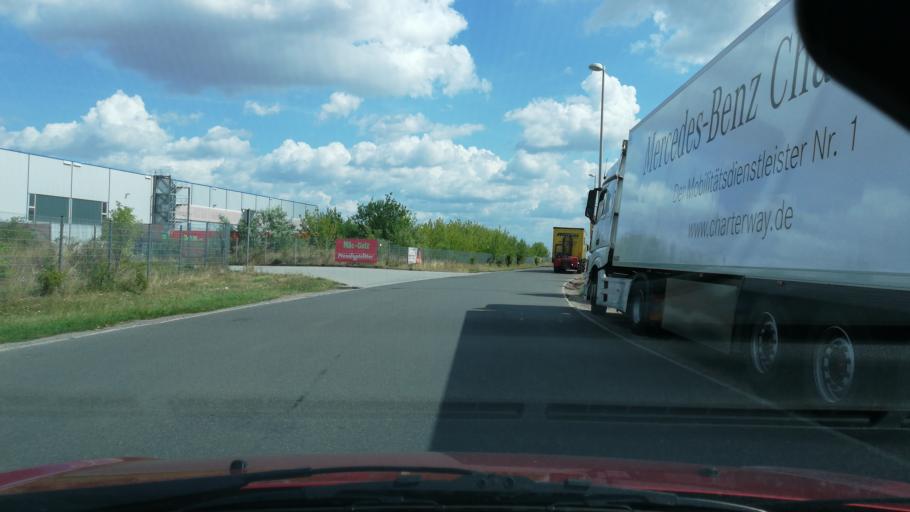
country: DE
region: Saxony-Anhalt
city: Landsberg
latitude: 51.5384
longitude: 12.1593
